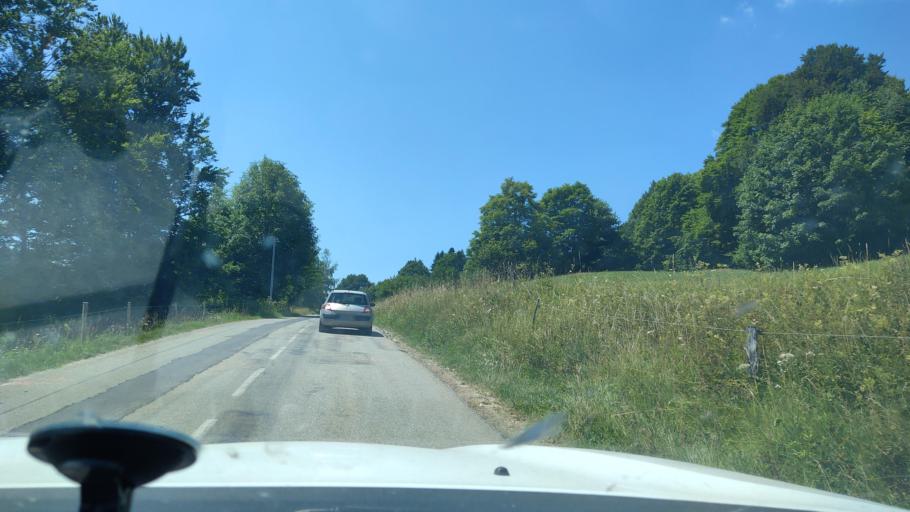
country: FR
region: Rhone-Alpes
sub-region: Departement de la Savoie
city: Mery
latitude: 45.6514
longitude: 6.0249
